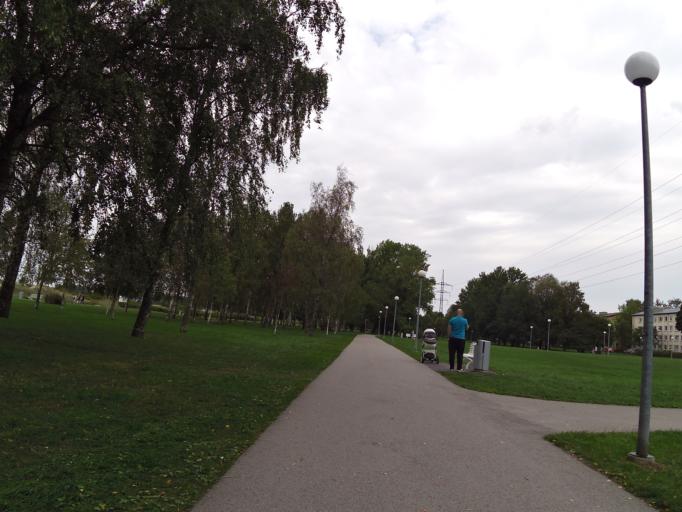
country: EE
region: Harju
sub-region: Tallinna linn
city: Tallinn
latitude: 59.4454
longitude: 24.6858
